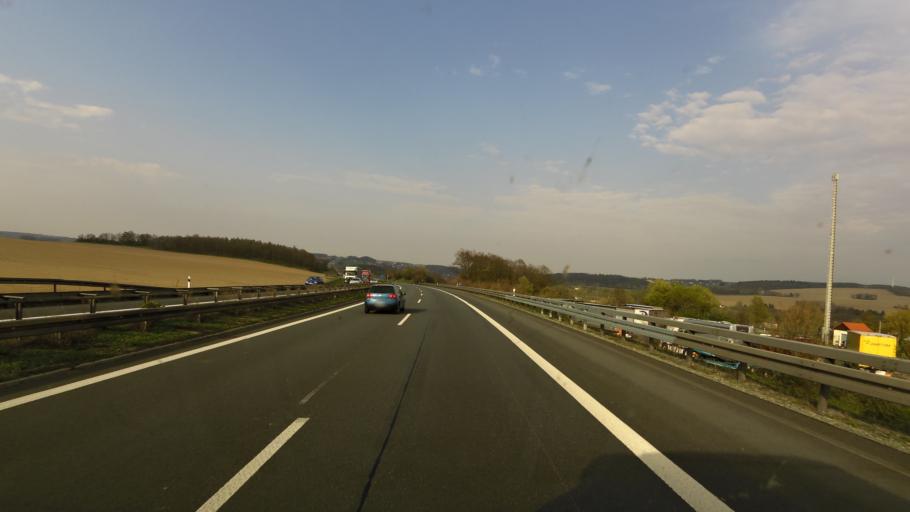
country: DE
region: Saxony
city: Neuensalz
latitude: 50.5071
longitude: 12.2150
